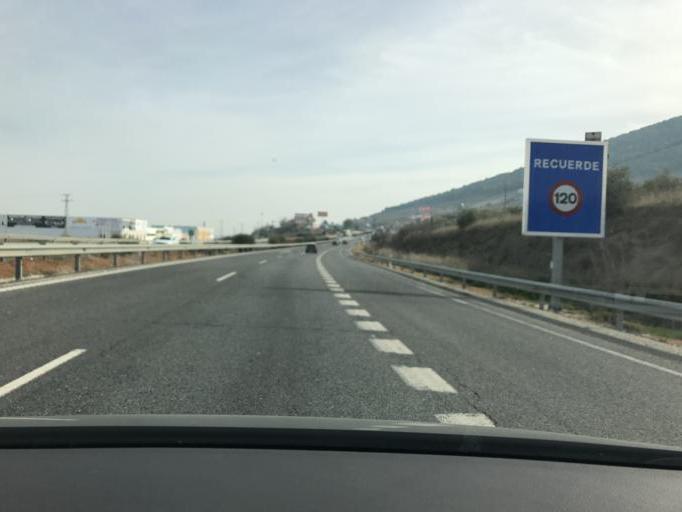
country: ES
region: Andalusia
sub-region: Provincia de Granada
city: Loja
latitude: 37.1666
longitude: -4.1764
